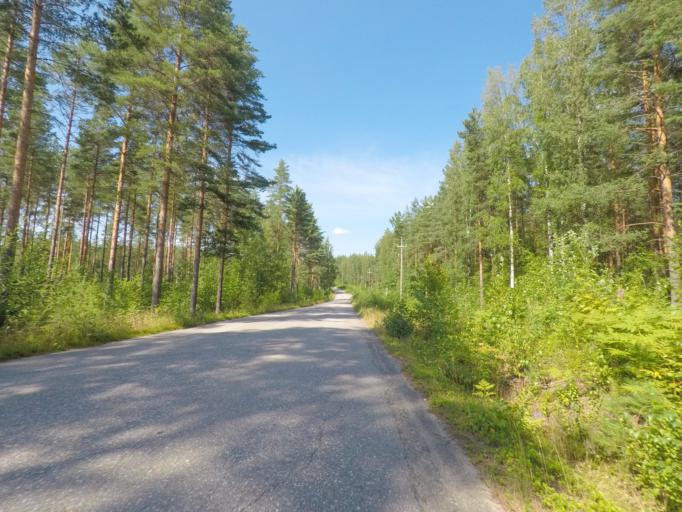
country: FI
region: Southern Savonia
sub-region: Mikkeli
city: Puumala
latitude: 61.4401
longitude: 28.1657
